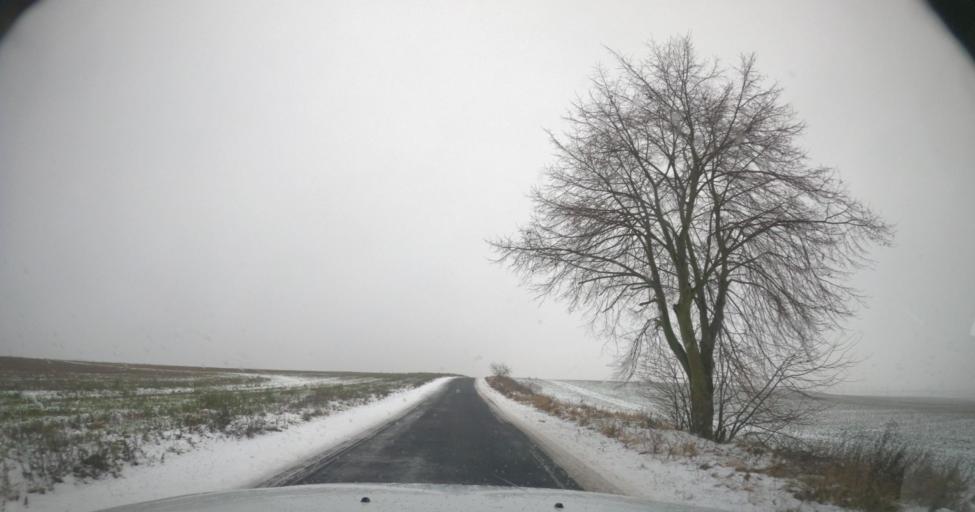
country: PL
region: West Pomeranian Voivodeship
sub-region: Powiat gryficki
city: Gryfice
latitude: 53.8840
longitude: 15.1388
